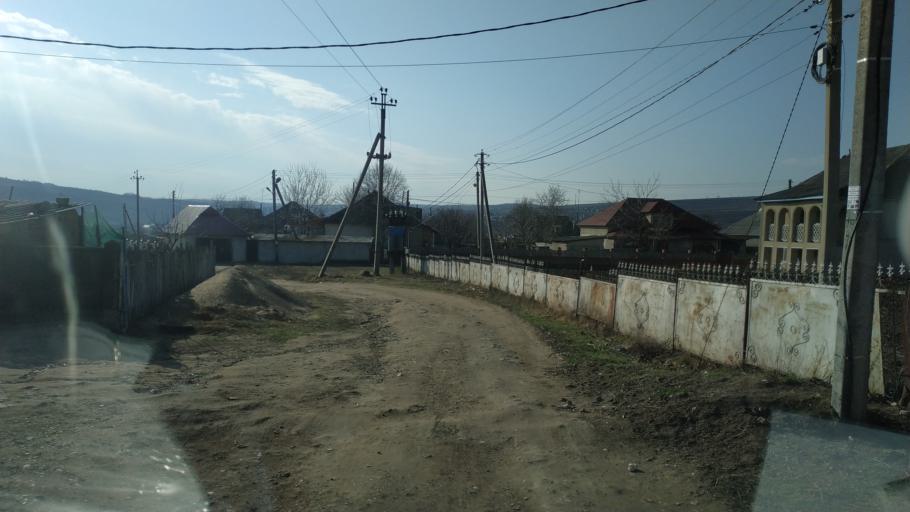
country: MD
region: Chisinau
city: Singera
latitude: 46.6874
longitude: 29.0411
